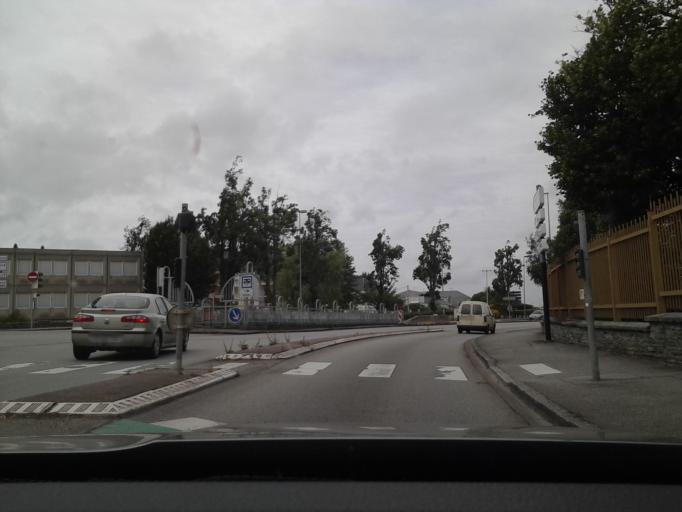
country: FR
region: Lower Normandy
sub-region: Departement de la Manche
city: Equeurdreville-Hainneville
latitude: 49.6467
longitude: -1.6423
